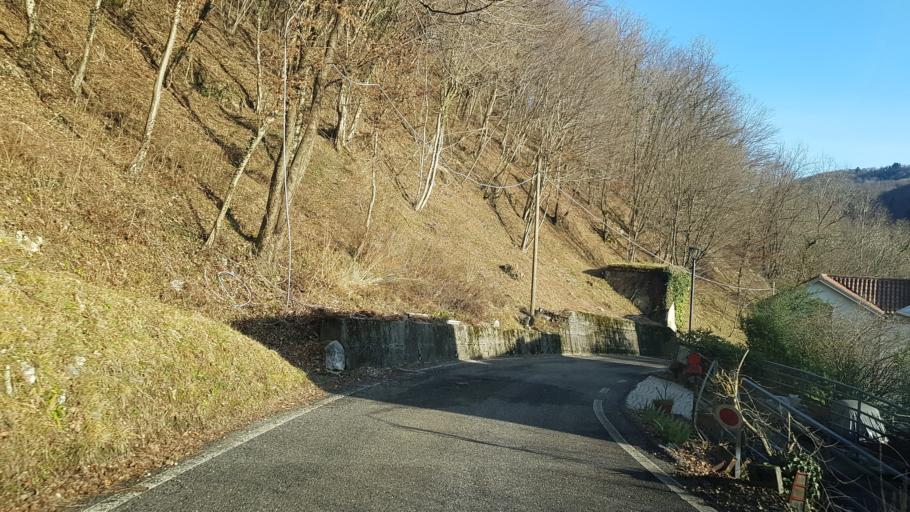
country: IT
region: Friuli Venezia Giulia
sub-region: Provincia di Udine
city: Clodig
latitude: 46.1574
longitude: 13.5864
